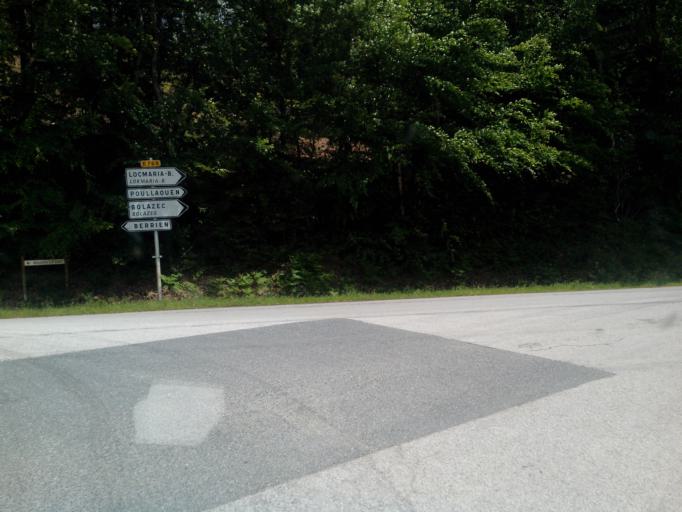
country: FR
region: Brittany
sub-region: Departement du Finistere
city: Huelgoat
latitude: 48.3651
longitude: -3.7131
